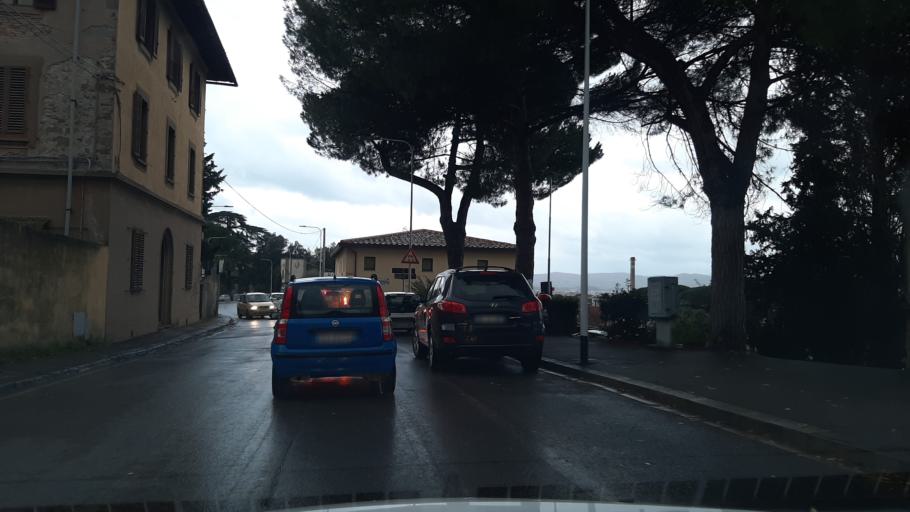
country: IT
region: Tuscany
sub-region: Province of Florence
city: Florence
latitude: 43.8118
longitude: 11.2501
